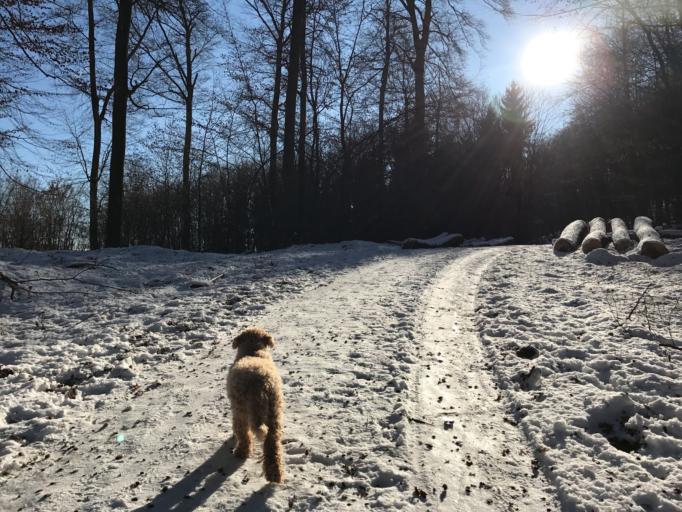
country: DE
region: Hesse
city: Eppstein
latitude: 50.1299
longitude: 8.3928
